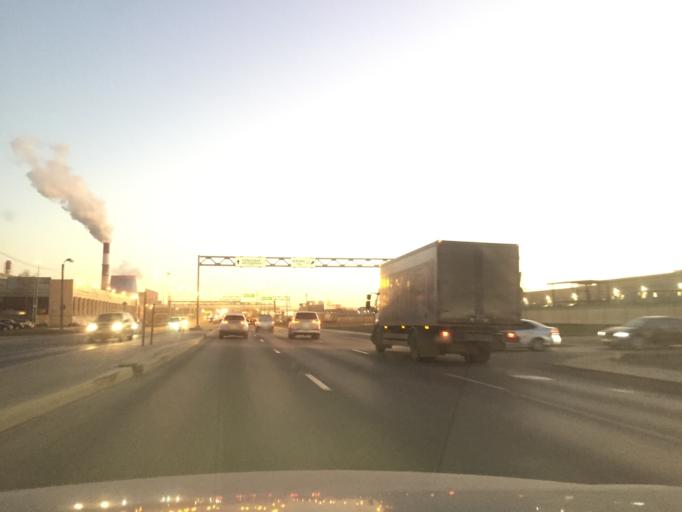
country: RU
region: St.-Petersburg
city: Obukhovo
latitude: 59.8374
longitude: 30.4378
